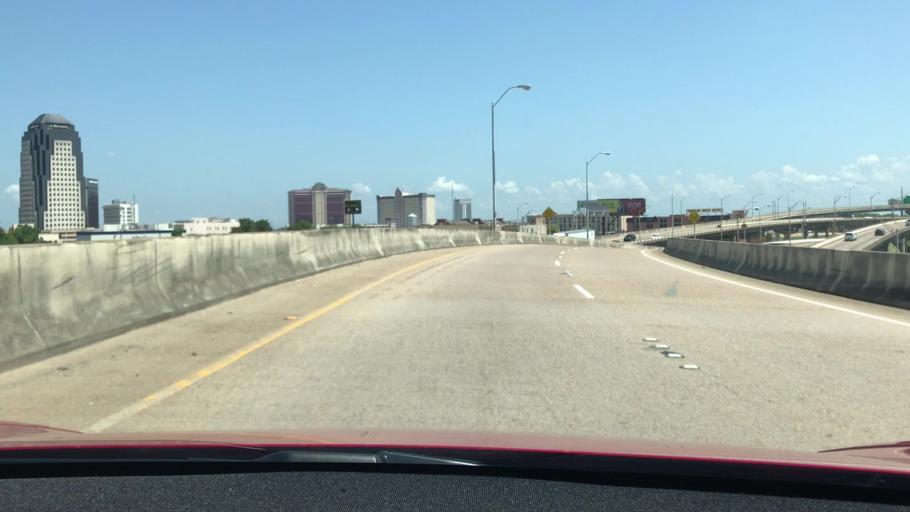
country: US
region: Louisiana
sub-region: Bossier Parish
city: Bossier City
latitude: 32.5071
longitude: -93.7453
